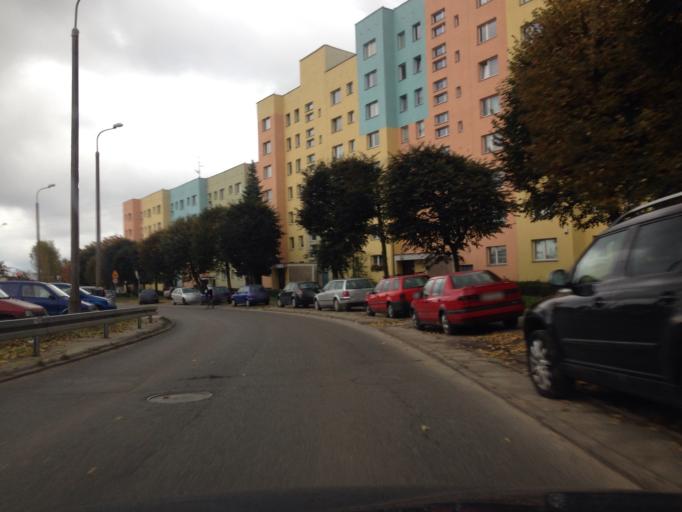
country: PL
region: Pomeranian Voivodeship
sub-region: Gdansk
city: Gdansk
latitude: 54.3945
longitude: 18.6141
